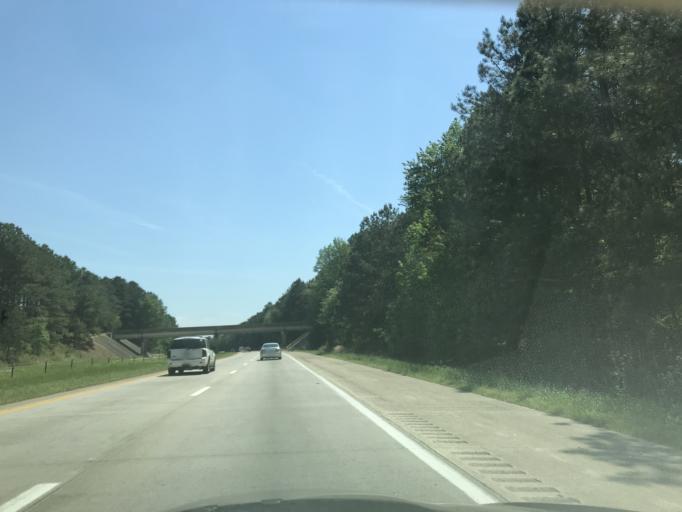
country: US
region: North Carolina
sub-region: Johnston County
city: Benson
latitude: 35.4736
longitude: -78.5497
